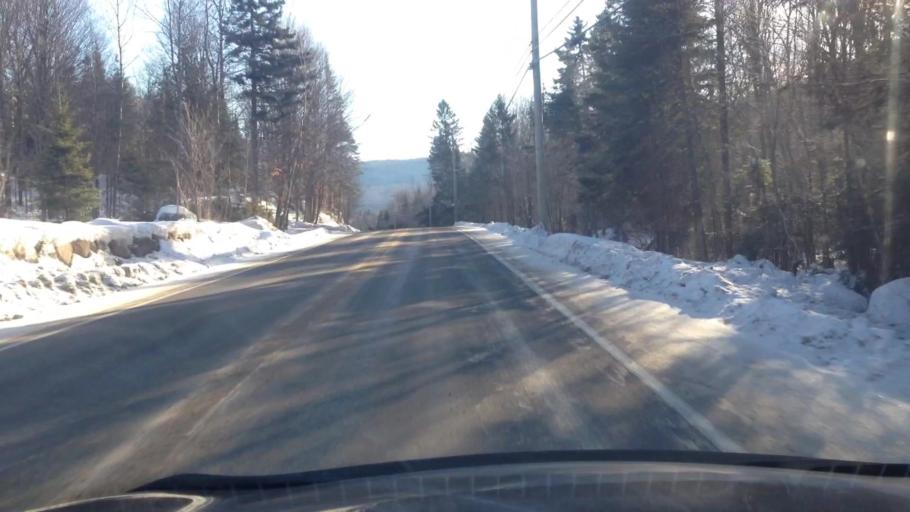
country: CA
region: Quebec
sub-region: Laurentides
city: Sainte-Agathe-des-Monts
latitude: 45.9095
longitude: -74.3331
